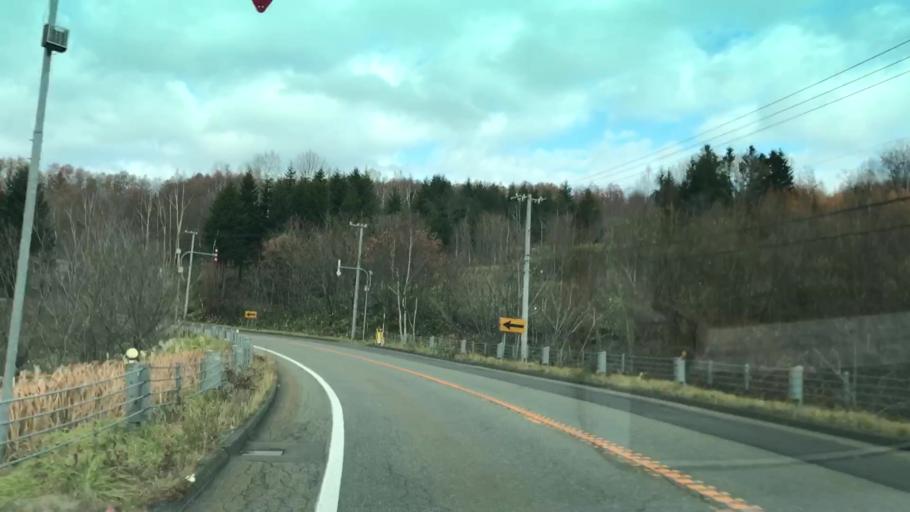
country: JP
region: Hokkaido
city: Shimo-furano
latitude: 42.8883
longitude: 142.4366
